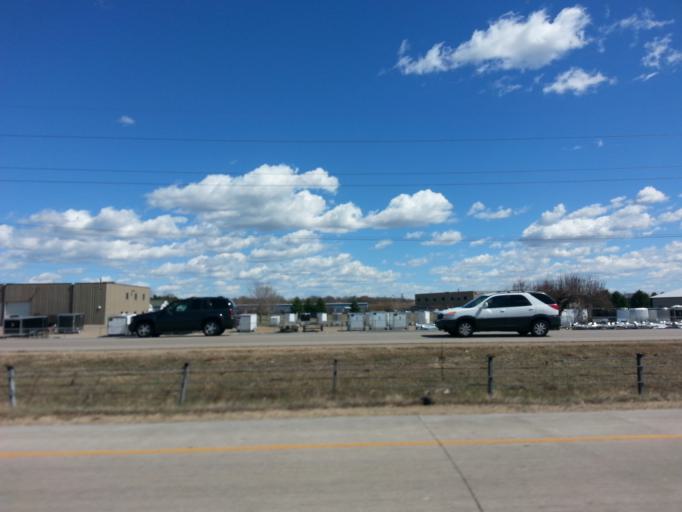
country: US
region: Minnesota
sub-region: Dakota County
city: Hastings
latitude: 44.7728
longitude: -92.8632
